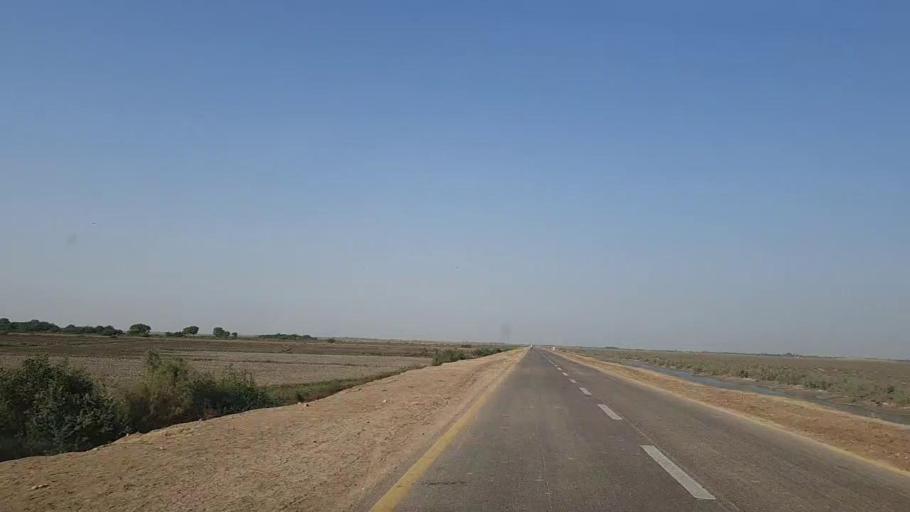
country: PK
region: Sindh
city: Jati
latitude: 24.4838
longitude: 68.3738
